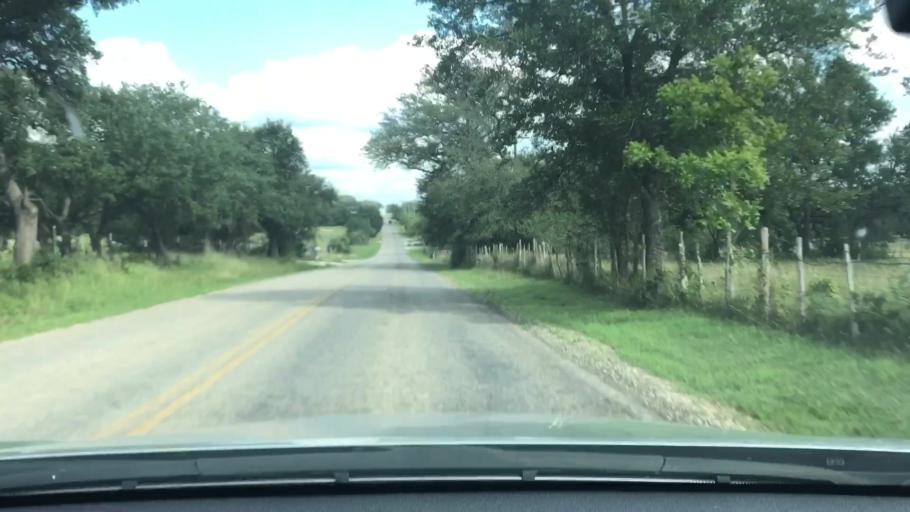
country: US
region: Texas
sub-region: Bexar County
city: Fair Oaks Ranch
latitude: 29.7862
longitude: -98.6689
